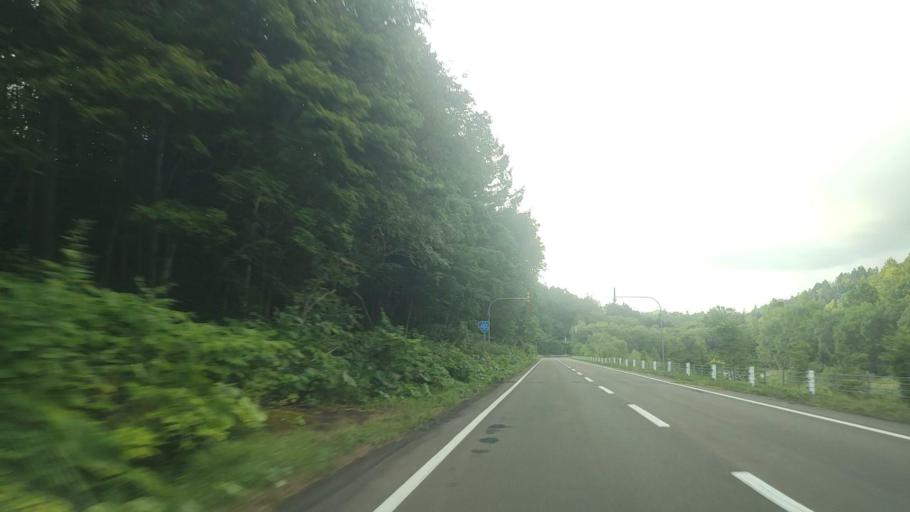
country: JP
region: Hokkaido
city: Bibai
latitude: 43.1236
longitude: 142.1030
